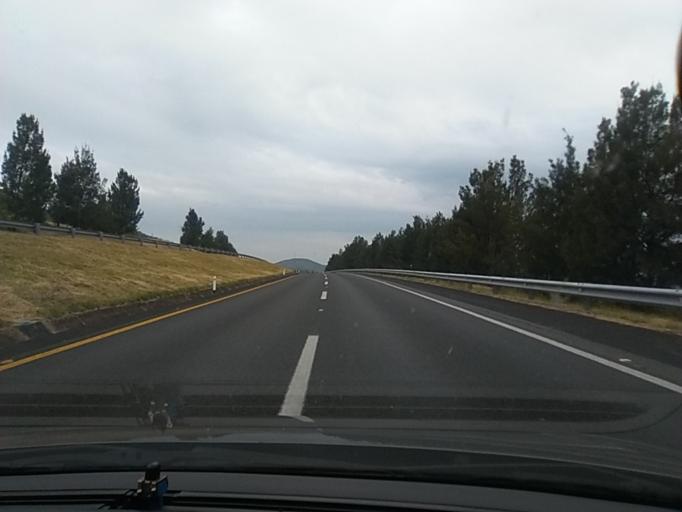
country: MX
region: Michoacan
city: Churintzio
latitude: 20.0976
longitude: -102.0248
